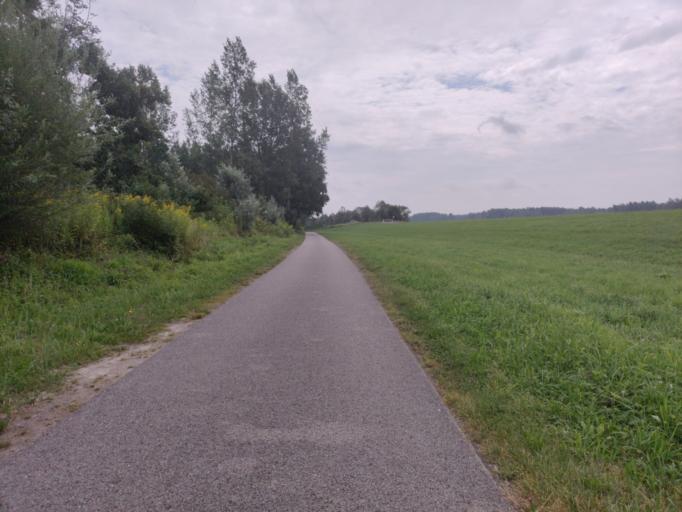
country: AT
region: Upper Austria
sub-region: Politischer Bezirk Perg
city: Perg
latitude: 48.2052
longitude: 14.6046
